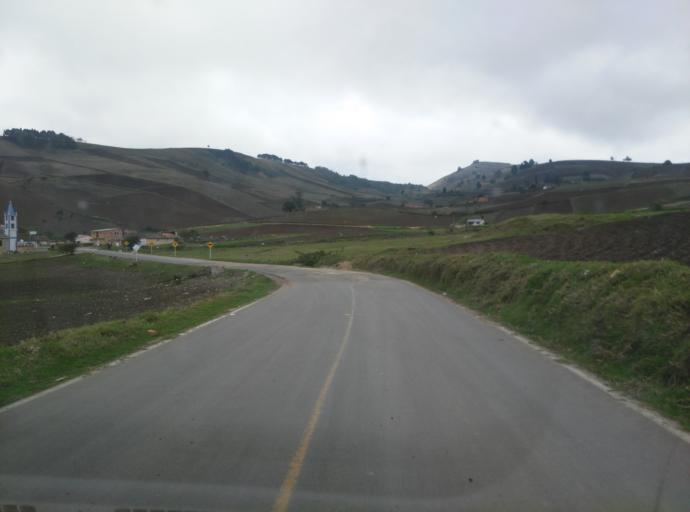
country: CO
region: Boyaca
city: Siachoque
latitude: 5.5002
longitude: -73.2905
